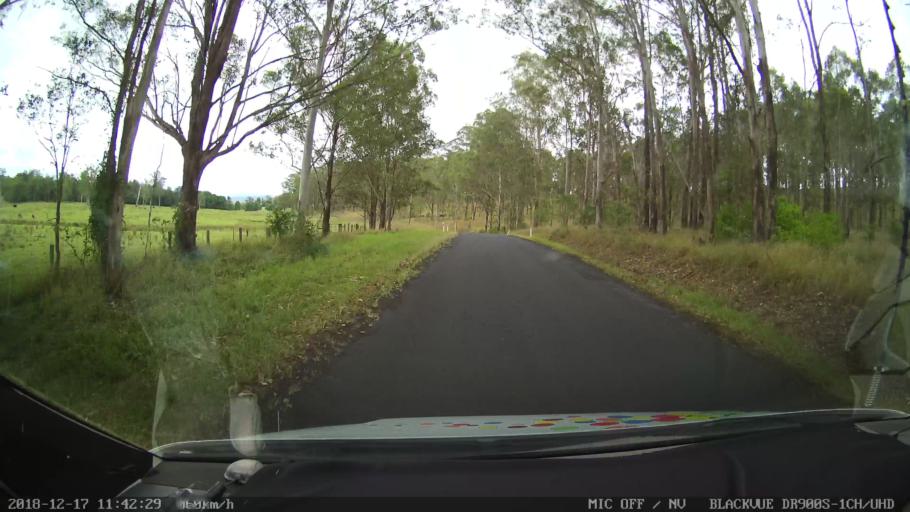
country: AU
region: New South Wales
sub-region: Kyogle
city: Kyogle
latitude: -28.6683
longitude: 152.5916
